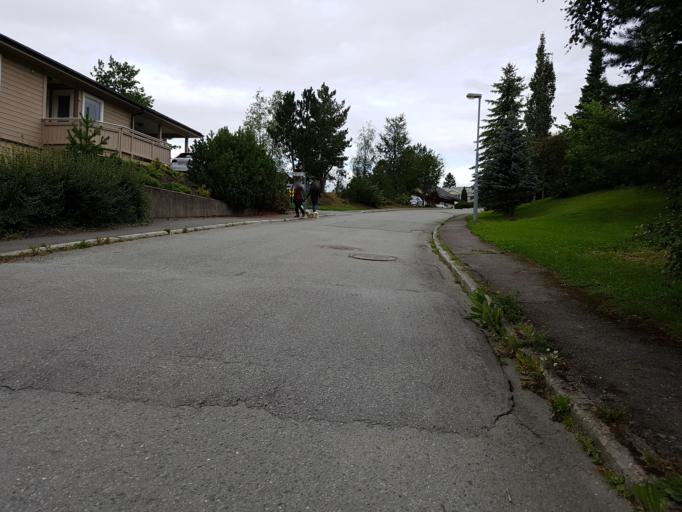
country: NO
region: Sor-Trondelag
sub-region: Trondheim
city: Trondheim
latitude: 63.3987
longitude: 10.4451
